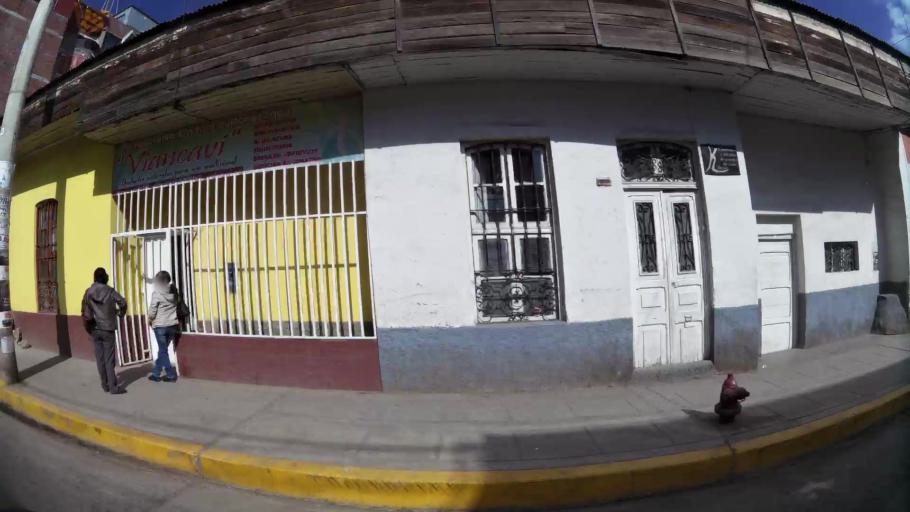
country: PE
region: Junin
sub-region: Provincia de Huancayo
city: Huancayo
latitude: -12.0654
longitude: -75.2099
